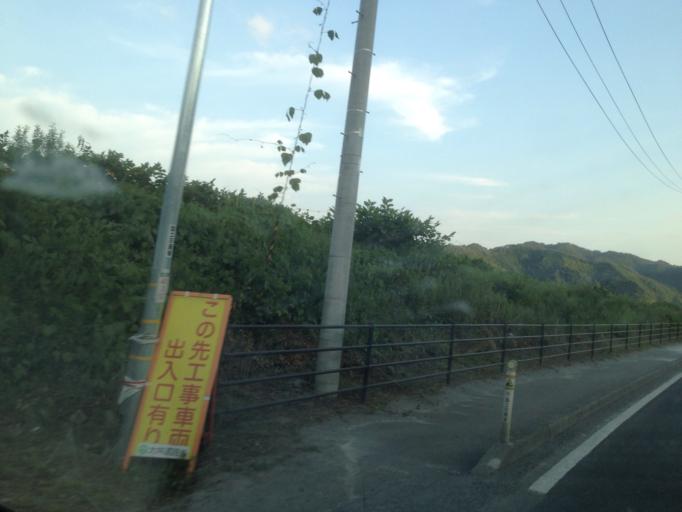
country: JP
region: Iwate
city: Otsuchi
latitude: 39.3391
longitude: 141.8936
